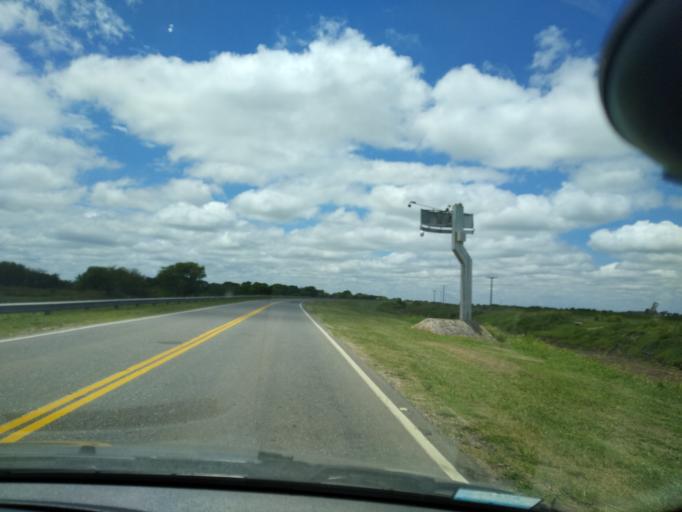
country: AR
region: Cordoba
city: Toledo
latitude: -31.6480
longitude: -64.0828
